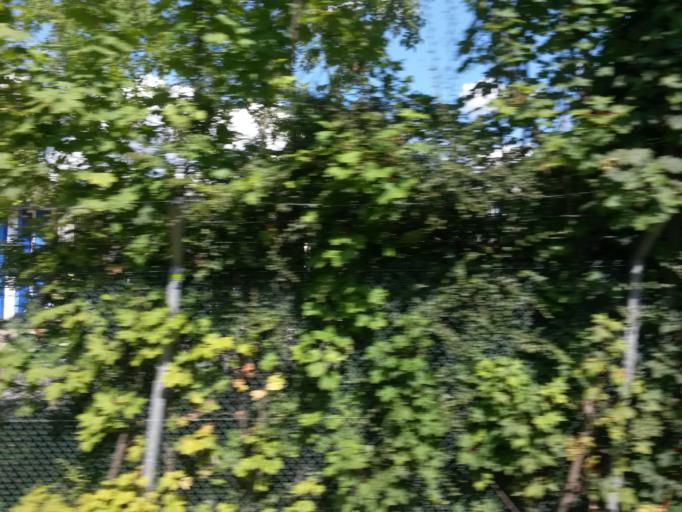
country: GB
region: England
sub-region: Greater London
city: Earlsfield
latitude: 51.4457
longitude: -0.1624
